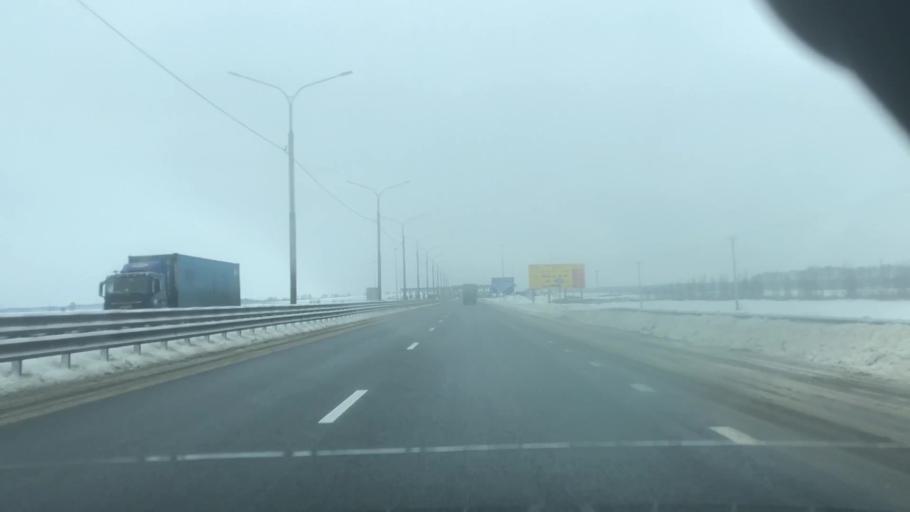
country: RU
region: Tula
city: Dubovka
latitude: 53.8838
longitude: 38.0512
